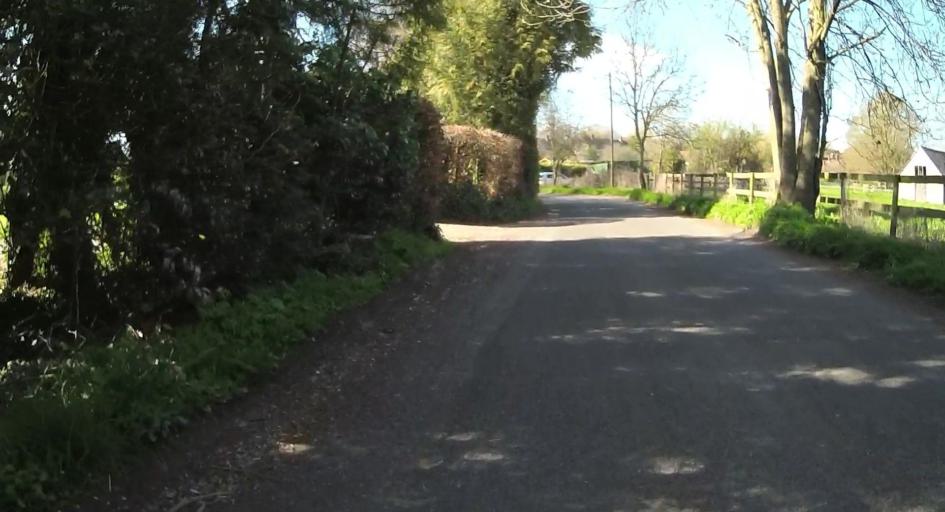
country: GB
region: England
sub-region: Hampshire
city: Abbotts Ann
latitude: 51.1318
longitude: -1.4855
